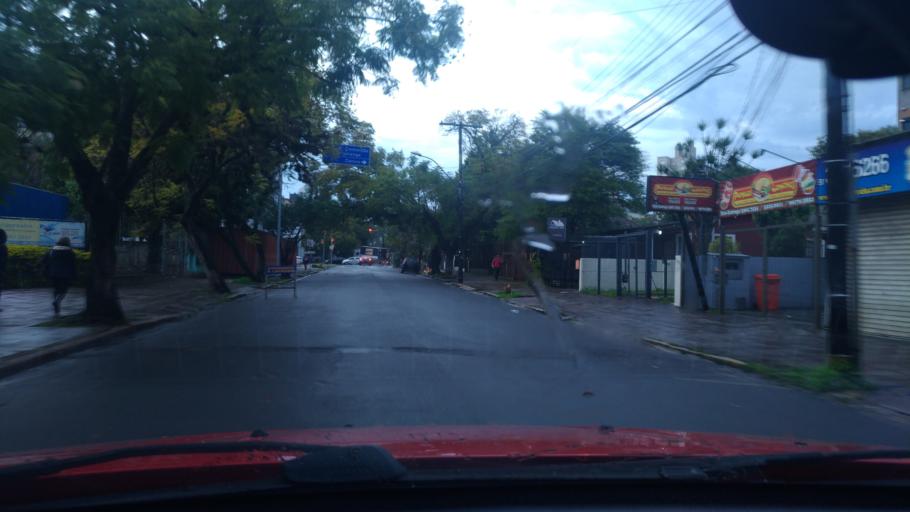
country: BR
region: Rio Grande do Sul
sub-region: Porto Alegre
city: Porto Alegre
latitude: -30.0124
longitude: -51.1650
